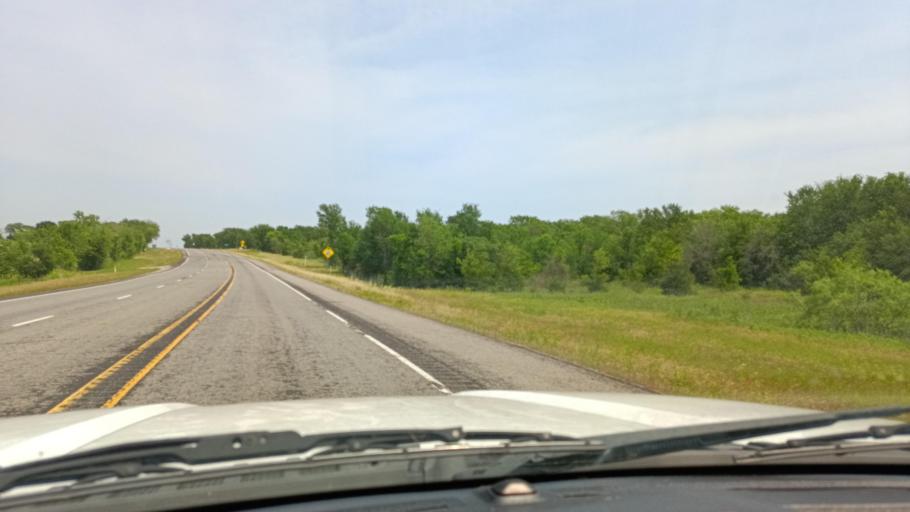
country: US
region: Texas
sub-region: Bell County
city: Rogers
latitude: 30.8780
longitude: -97.1423
